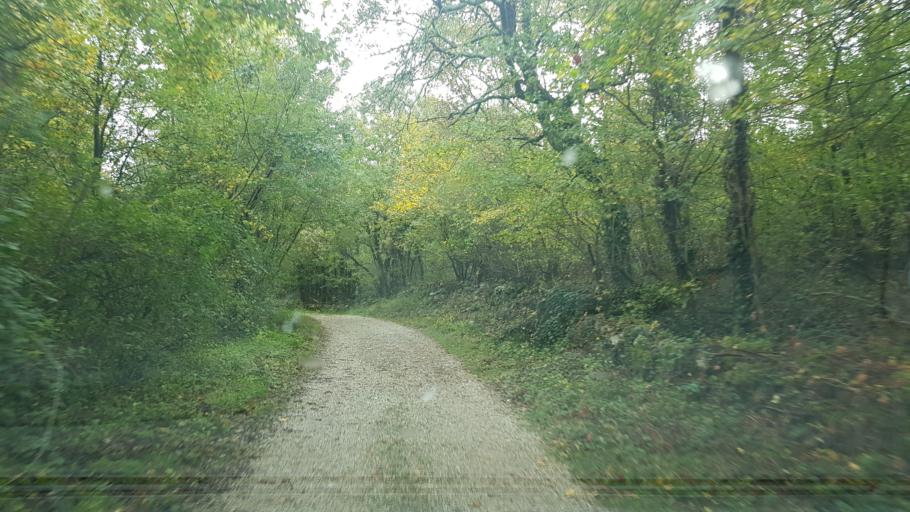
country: IT
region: Friuli Venezia Giulia
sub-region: Provincia di Gorizia
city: Monfalcone
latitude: 45.8177
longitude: 13.5290
